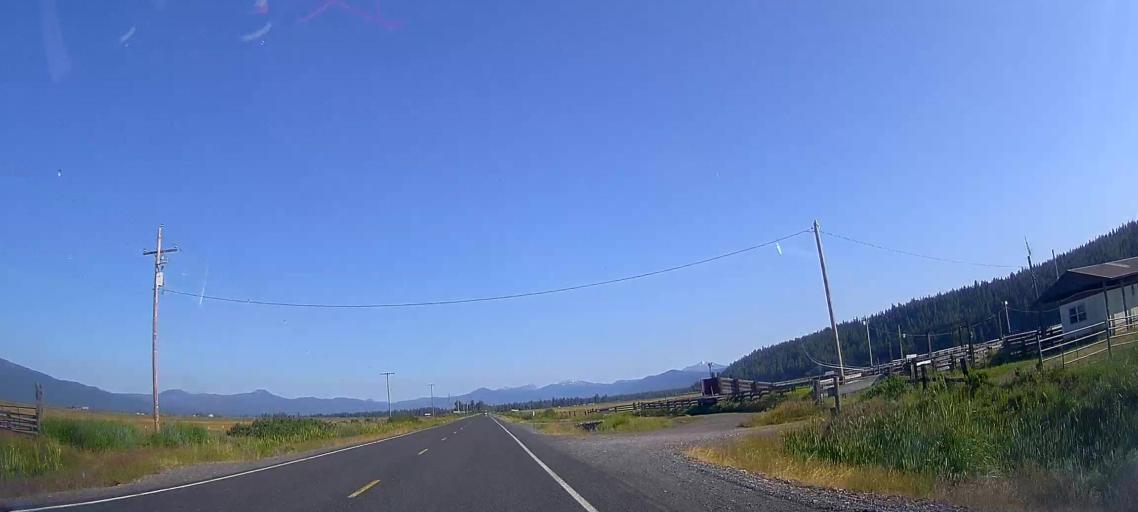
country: US
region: Oregon
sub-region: Klamath County
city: Klamath Falls
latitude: 42.6529
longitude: -121.9577
